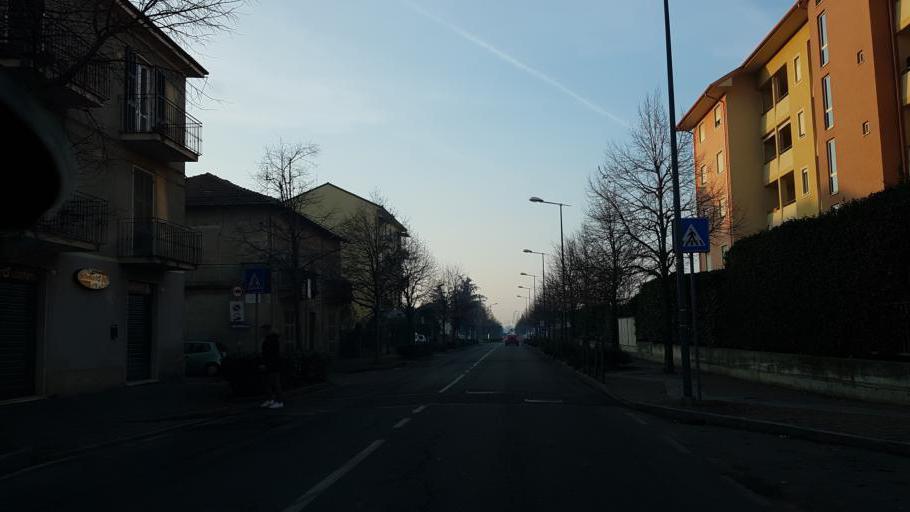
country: IT
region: Piedmont
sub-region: Provincia di Alessandria
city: Novi Ligure
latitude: 44.7645
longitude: 8.7763
